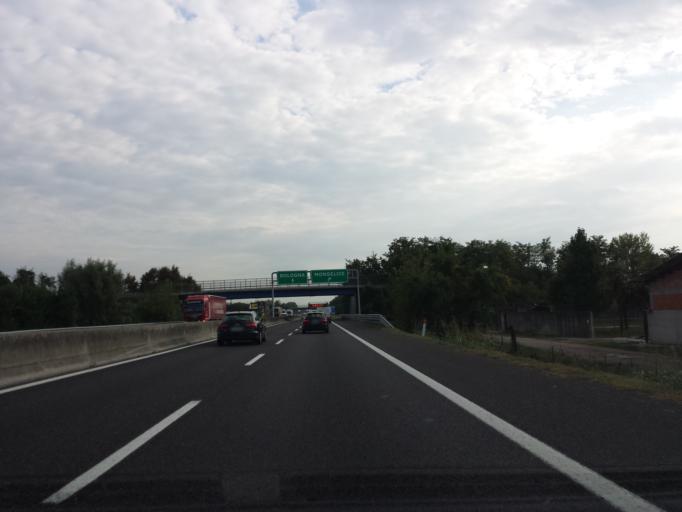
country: IT
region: Veneto
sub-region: Provincia di Padova
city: Pernumia
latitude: 45.2483
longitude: 11.7745
